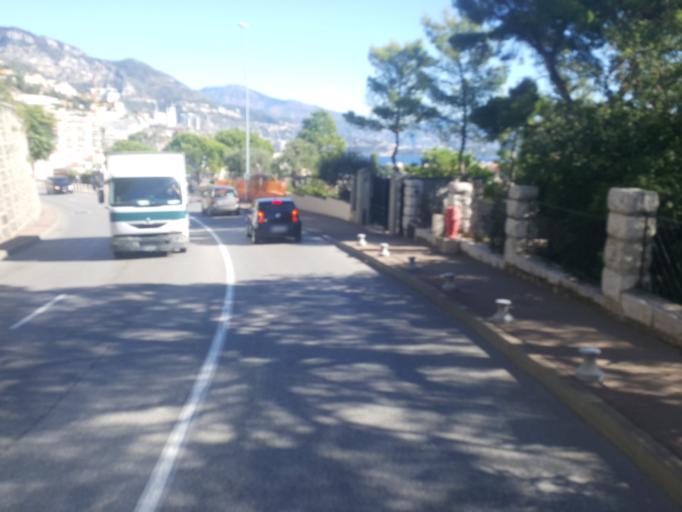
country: FR
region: Provence-Alpes-Cote d'Azur
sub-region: Departement des Alpes-Maritimes
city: Cap-d'Ail
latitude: 43.7244
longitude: 7.4061
